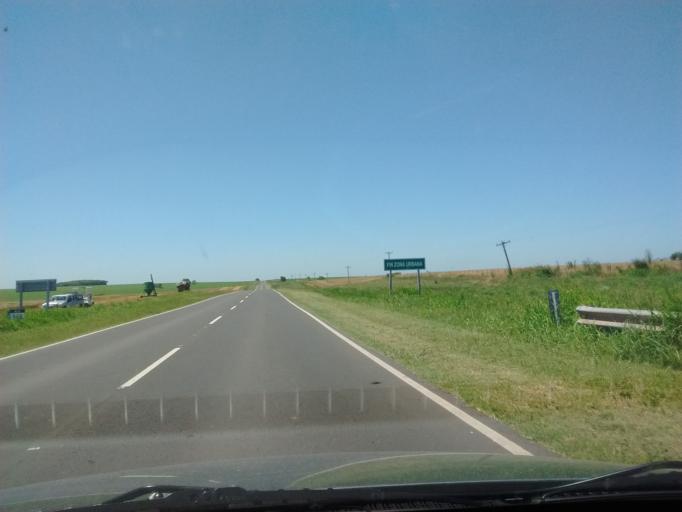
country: AR
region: Entre Rios
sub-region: Departamento de Victoria
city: Victoria
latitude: -32.7895
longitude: -59.9006
